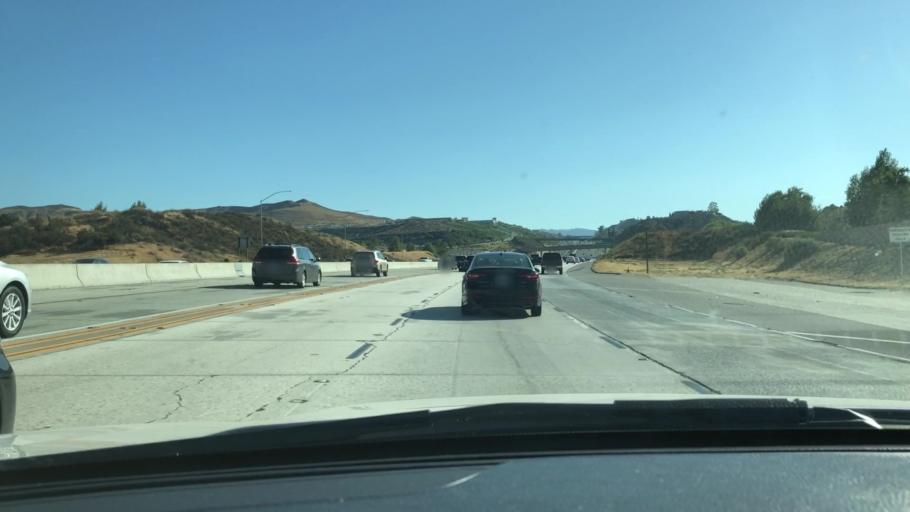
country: US
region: California
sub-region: Los Angeles County
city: Santa Clarita
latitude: 34.4062
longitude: -118.4494
